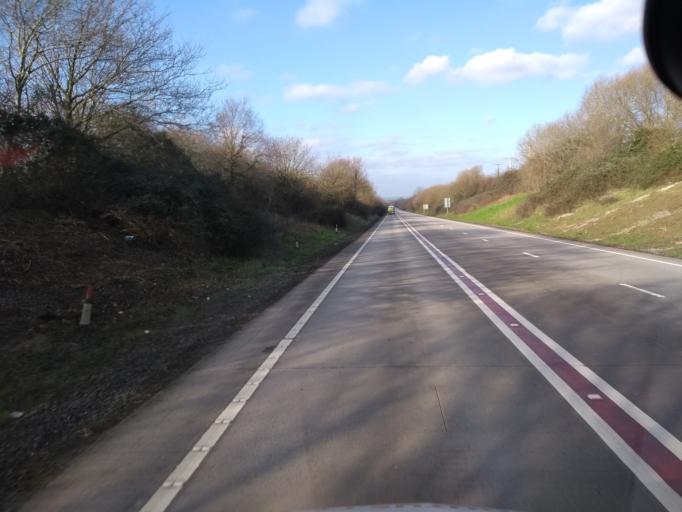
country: GB
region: England
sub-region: Somerset
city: Ilminster
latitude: 50.9349
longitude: -2.8699
